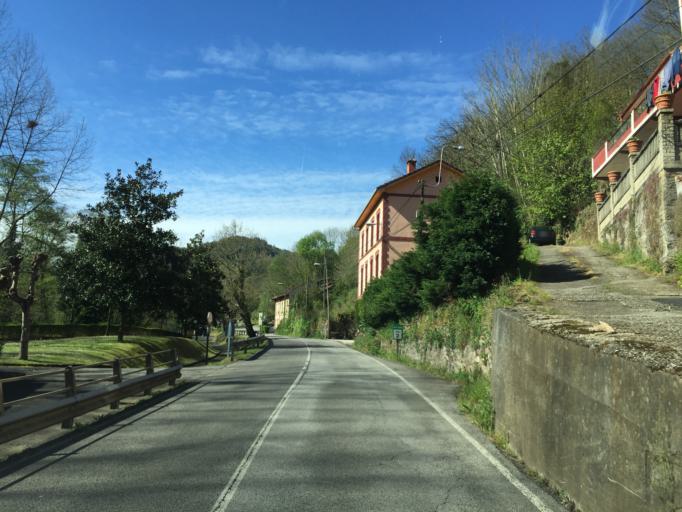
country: ES
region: Asturias
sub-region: Province of Asturias
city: Proaza
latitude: 43.3421
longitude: -5.9820
